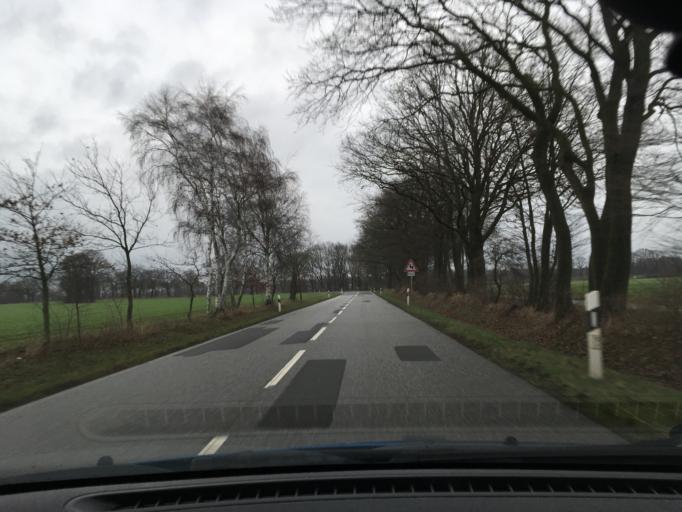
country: DE
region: Mecklenburg-Vorpommern
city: Nostorf
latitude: 53.3988
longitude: 10.6344
